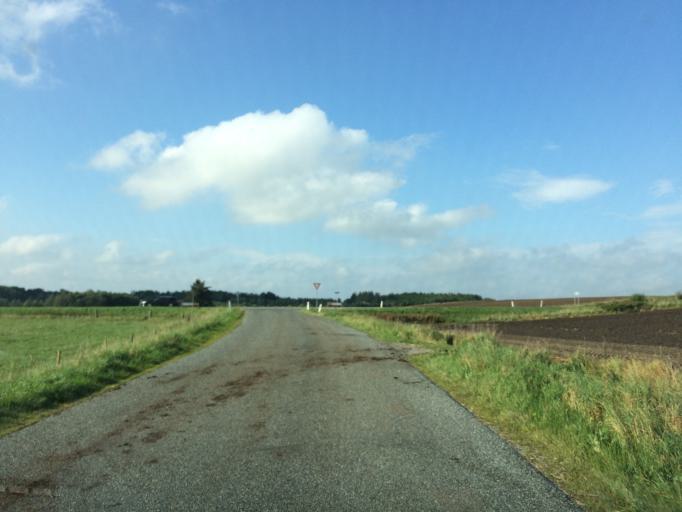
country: DK
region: Central Jutland
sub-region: Skive Kommune
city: Skive
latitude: 56.5054
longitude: 8.9564
